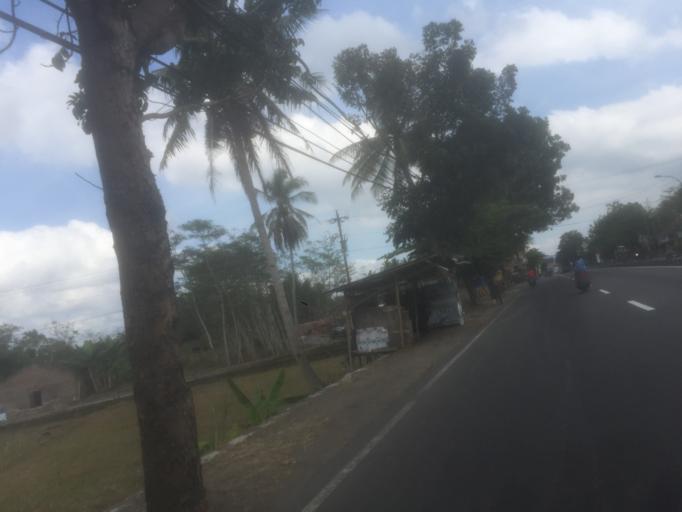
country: ID
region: Daerah Istimewa Yogyakarta
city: Sleman
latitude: -7.6625
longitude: 110.3293
